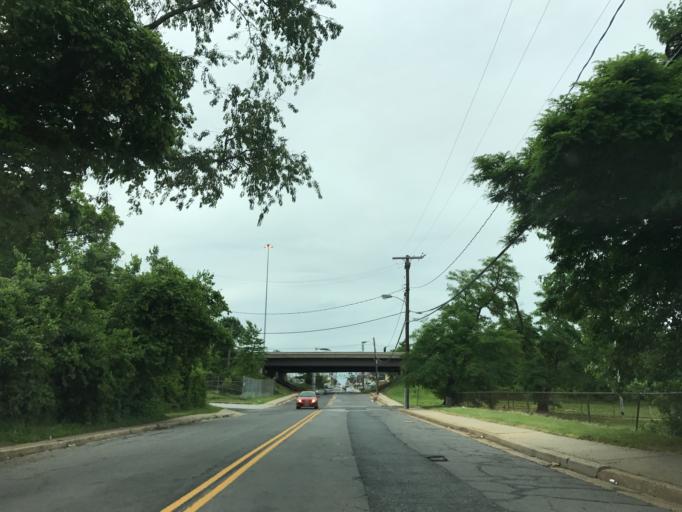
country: US
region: Maryland
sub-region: Baltimore County
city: Dundalk
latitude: 39.2830
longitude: -76.5406
